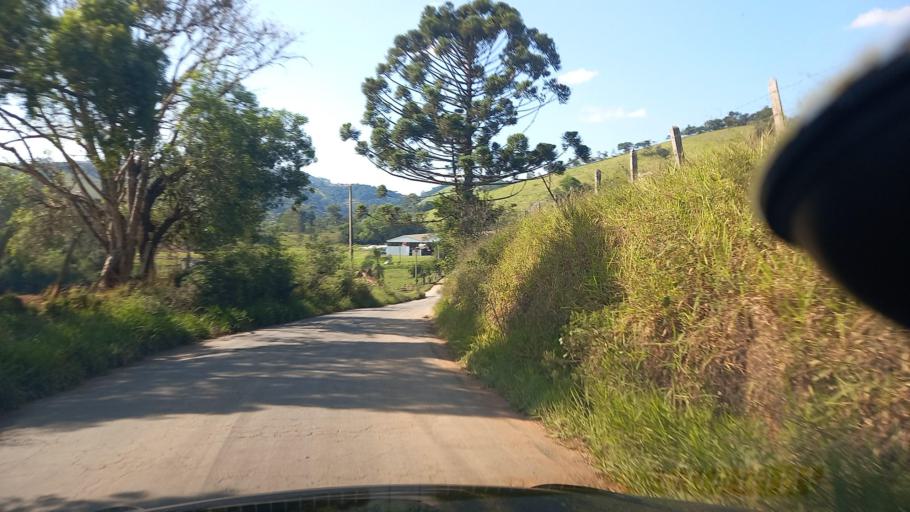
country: BR
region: Minas Gerais
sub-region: Camanducaia
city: Camanducaia
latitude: -22.7784
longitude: -46.1639
